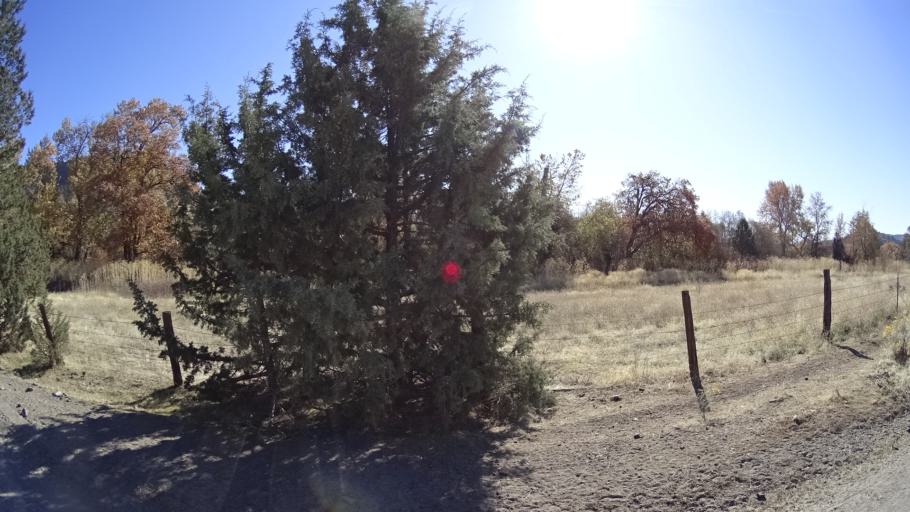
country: US
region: California
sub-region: Siskiyou County
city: Montague
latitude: 41.7328
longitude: -122.3515
